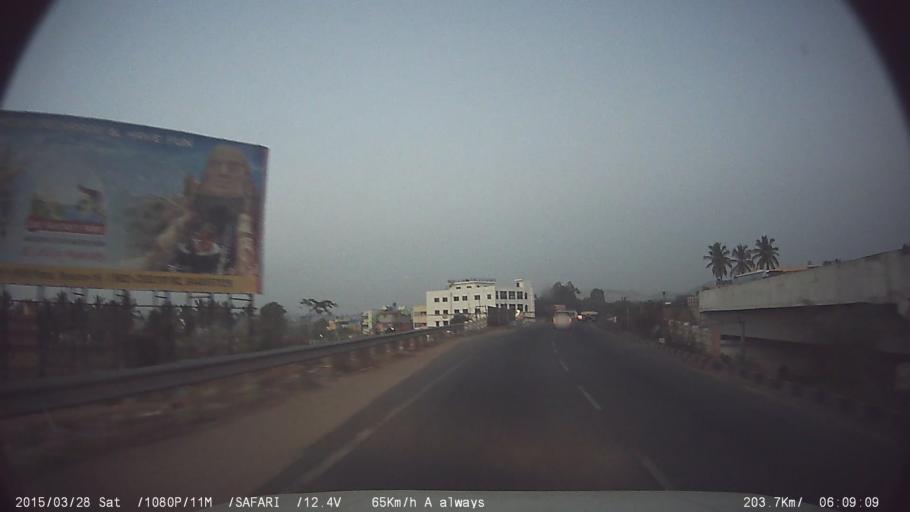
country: IN
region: Karnataka
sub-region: Ramanagara
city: Ramanagaram
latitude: 12.7971
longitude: 77.3881
